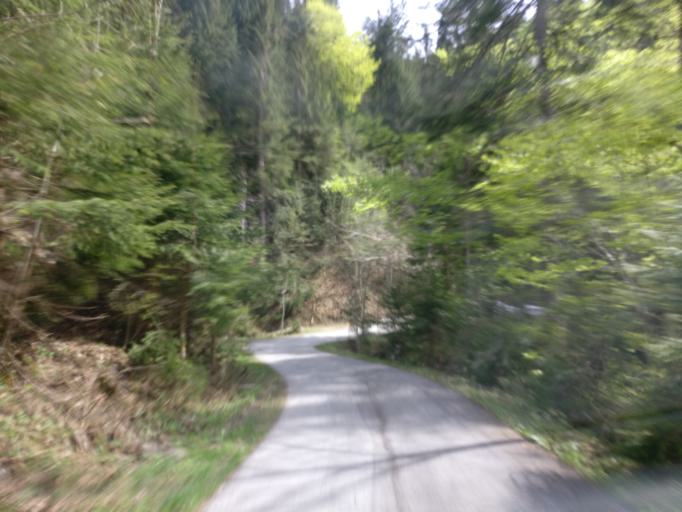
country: AT
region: Salzburg
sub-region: Politischer Bezirk Sankt Johann im Pongau
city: Pfarrwerfen
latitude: 47.4817
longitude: 13.2100
